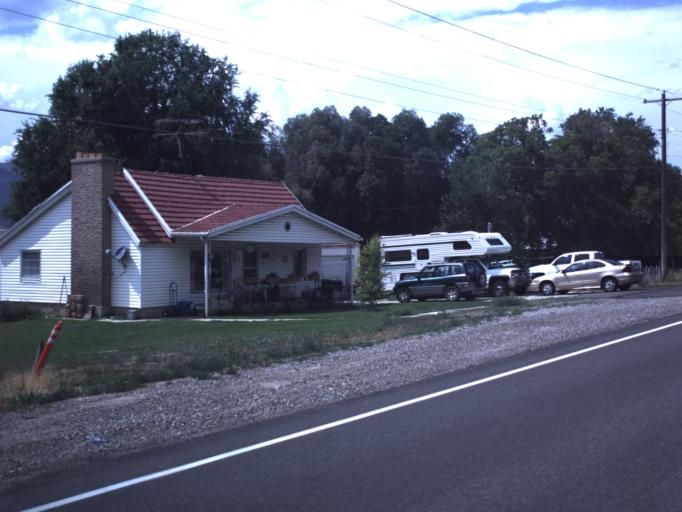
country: US
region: Utah
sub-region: Sanpete County
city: Moroni
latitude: 39.5297
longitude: -111.5906
